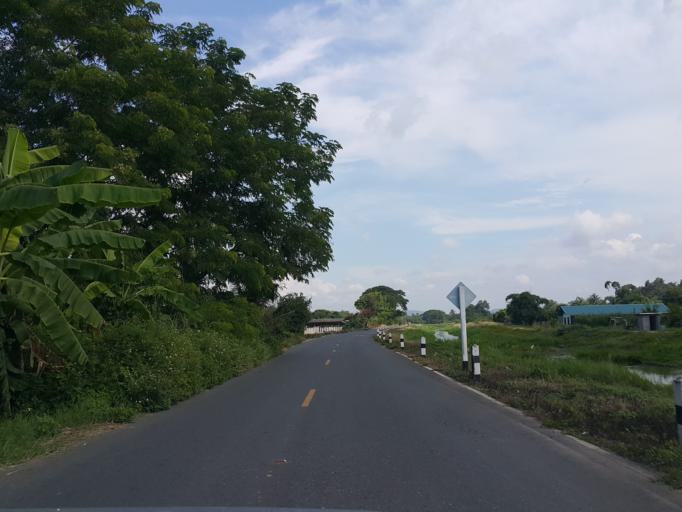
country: TH
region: Chiang Mai
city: Mae Taeng
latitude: 18.9846
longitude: 98.9793
